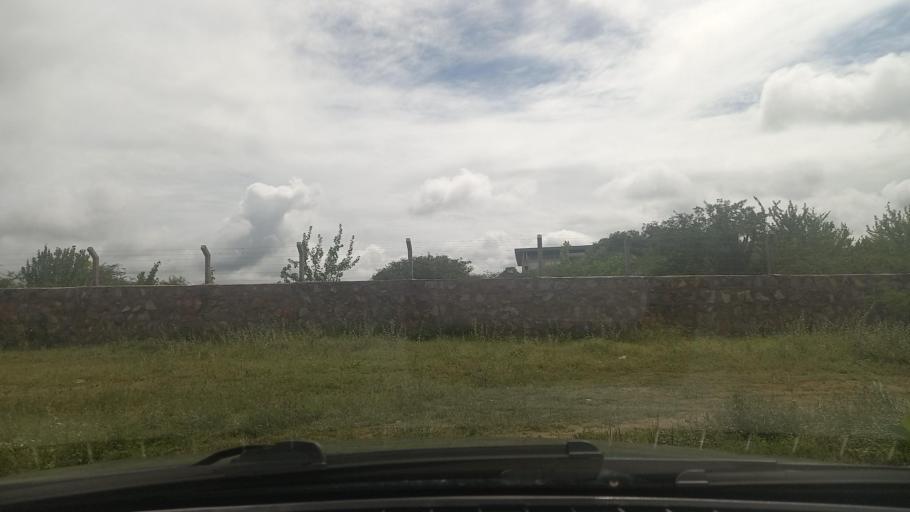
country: BR
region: Bahia
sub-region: Paulo Afonso
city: Paulo Afonso
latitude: -9.4011
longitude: -38.2458
